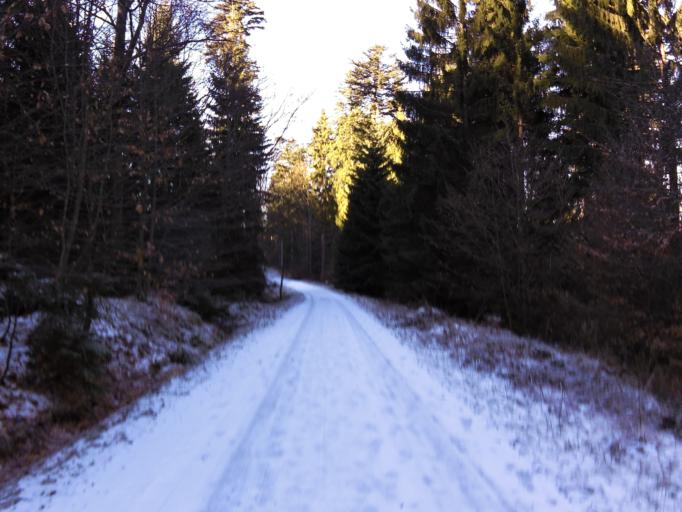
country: DE
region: Bavaria
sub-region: Upper Franconia
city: Bischofsgrun
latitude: 50.0417
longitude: 11.8279
